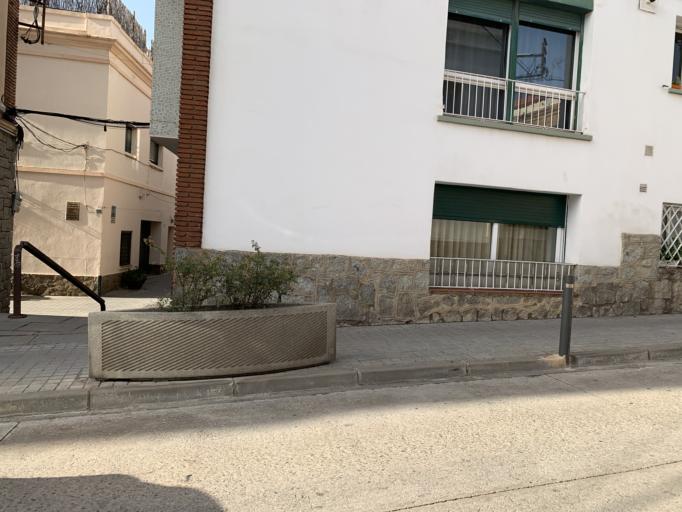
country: ES
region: Catalonia
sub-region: Provincia de Barcelona
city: El Masnou
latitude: 41.4802
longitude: 2.3191
